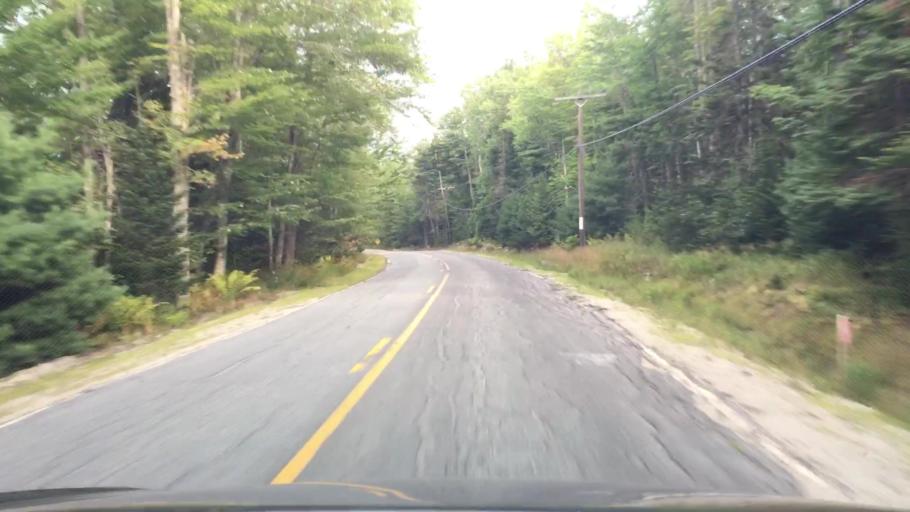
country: US
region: Maine
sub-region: Hancock County
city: Surry
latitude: 44.5007
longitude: -68.5723
